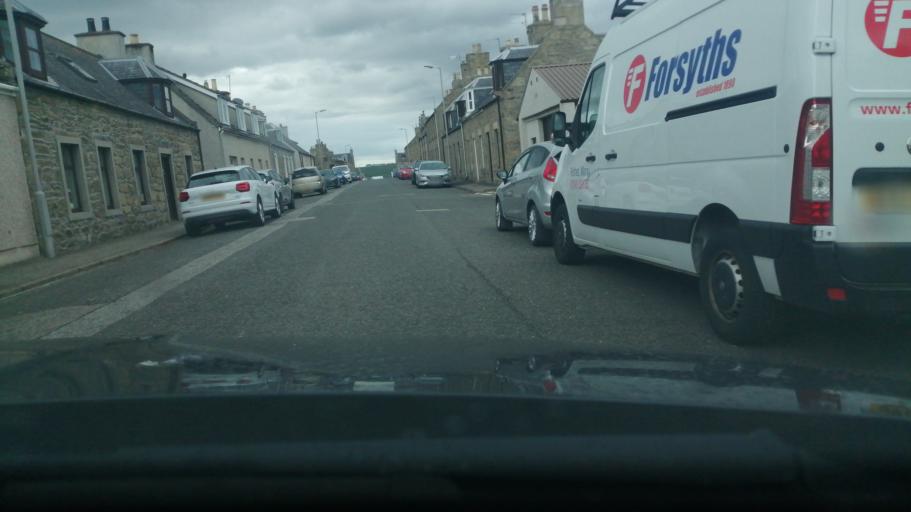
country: GB
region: Scotland
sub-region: Moray
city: Keith
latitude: 57.5367
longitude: -2.9528
